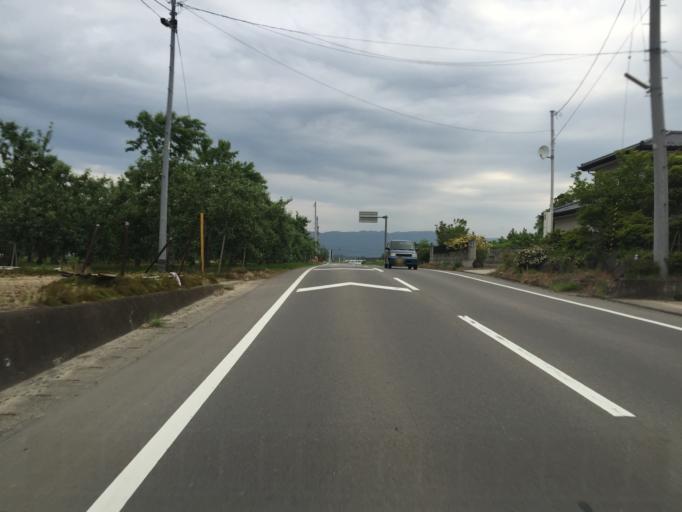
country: JP
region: Fukushima
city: Hobaramachi
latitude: 37.8264
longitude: 140.5361
